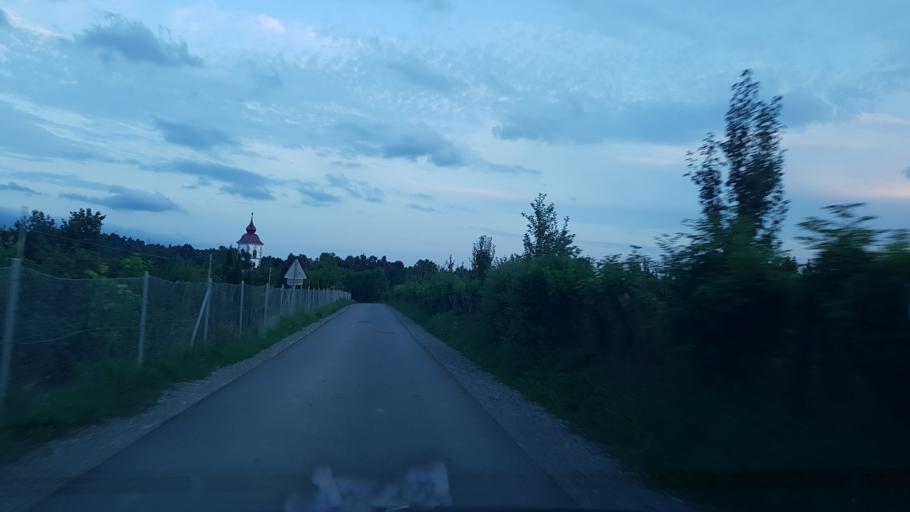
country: SI
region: Postojna
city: Postojna
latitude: 45.7433
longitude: 14.1837
